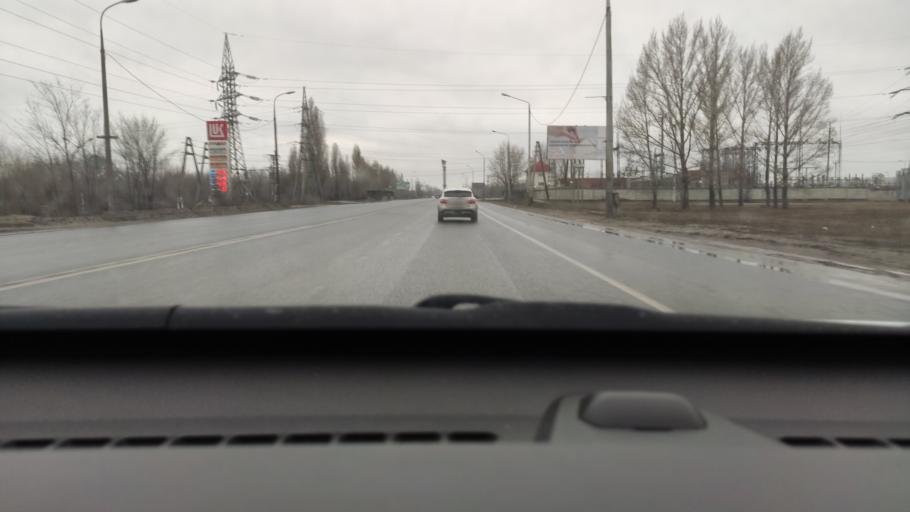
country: RU
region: Samara
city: Tol'yatti
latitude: 53.5575
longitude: 49.2839
